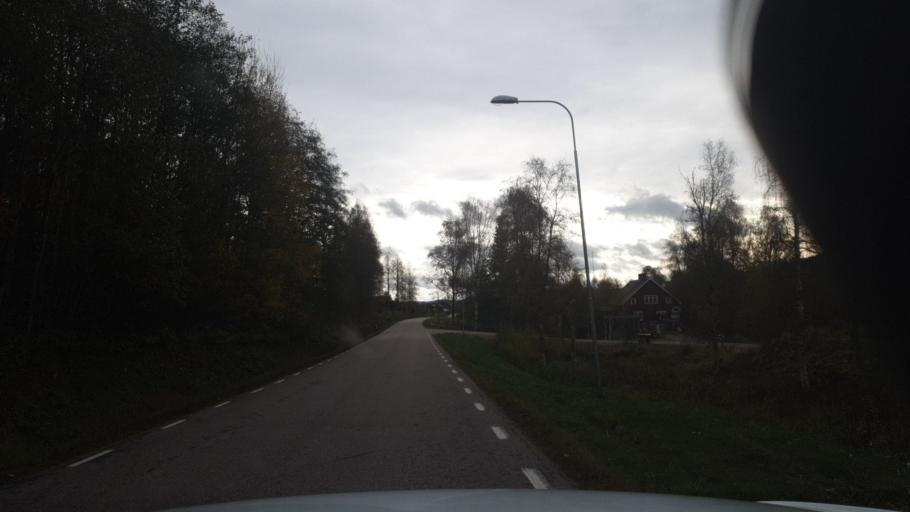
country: SE
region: Vaermland
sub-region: Arvika Kommun
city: Arvika
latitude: 59.7585
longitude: 12.7962
